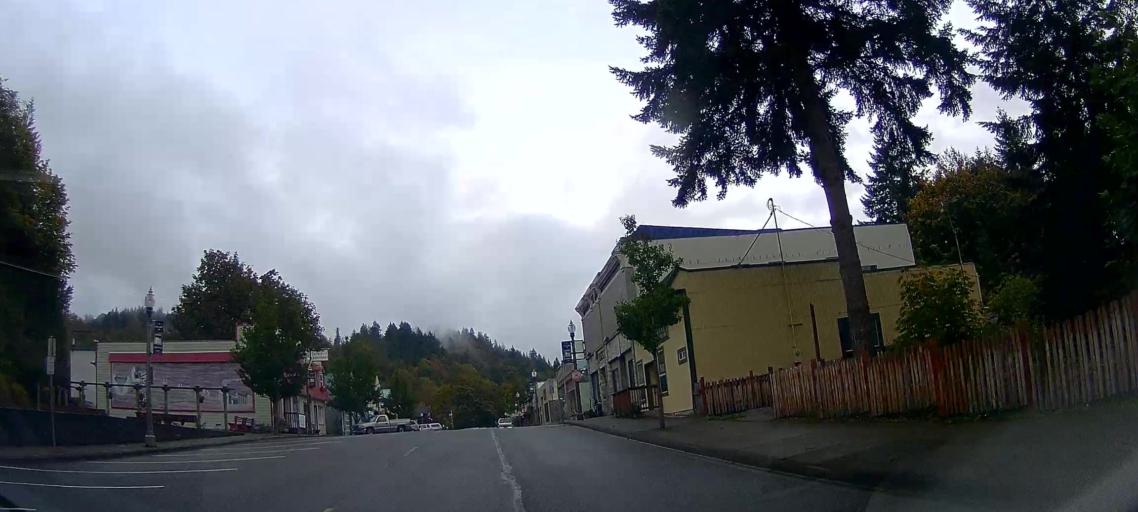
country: US
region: Washington
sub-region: Snohomish County
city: Darrington
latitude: 48.5388
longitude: -121.7478
